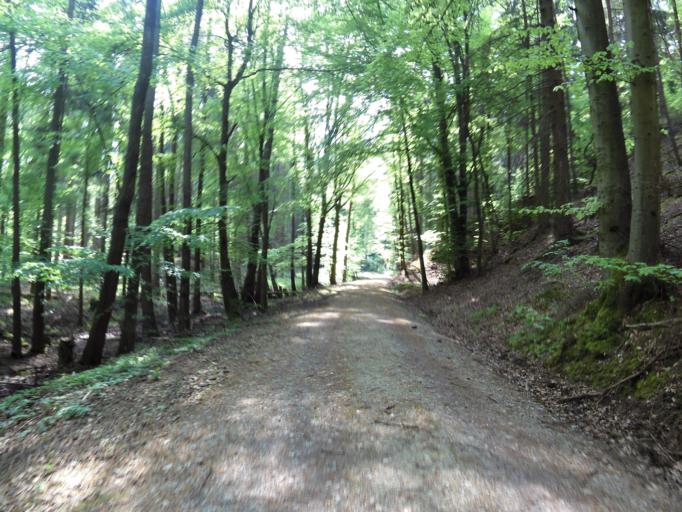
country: DE
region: Thuringia
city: Eisenach
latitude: 50.9569
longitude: 10.2920
